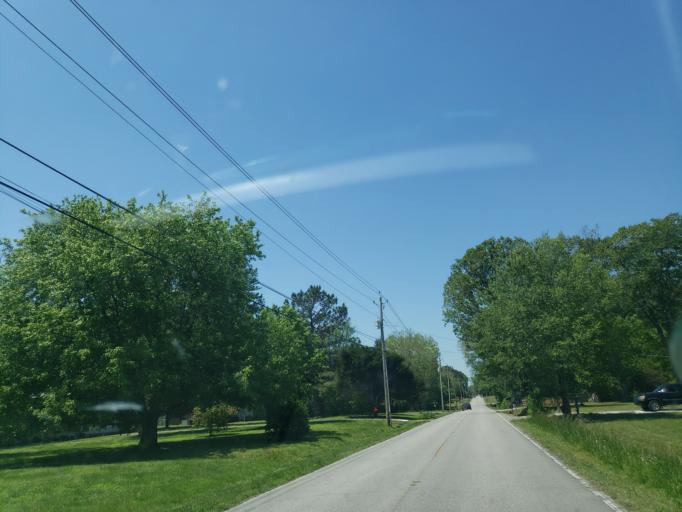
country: US
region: Alabama
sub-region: Madison County
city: Hazel Green
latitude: 34.9624
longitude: -86.6836
